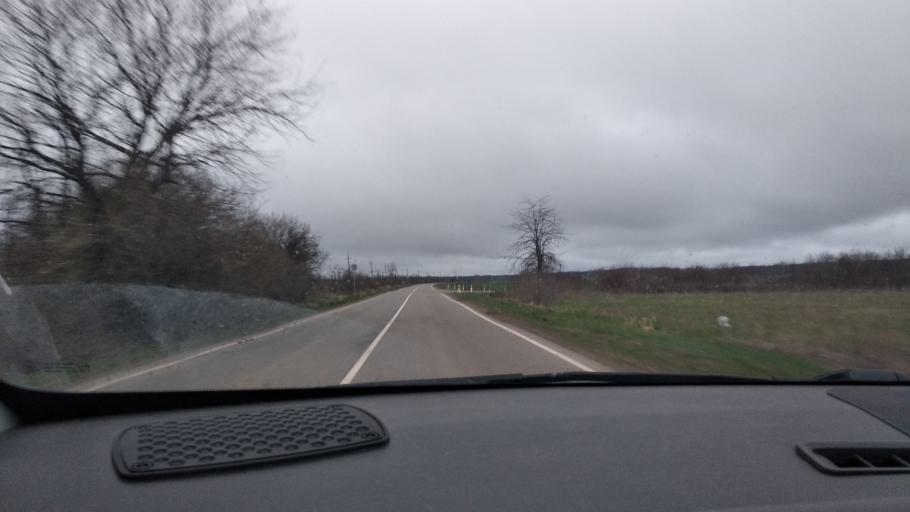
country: RU
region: Krasnodarskiy
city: Afipskiy
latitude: 44.8994
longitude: 38.7880
